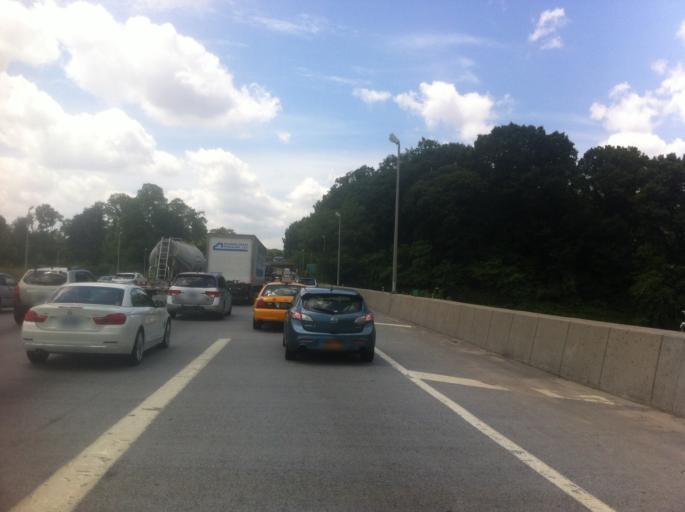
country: US
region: New York
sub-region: Nassau County
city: Lake Success
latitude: 40.7541
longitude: -73.7440
